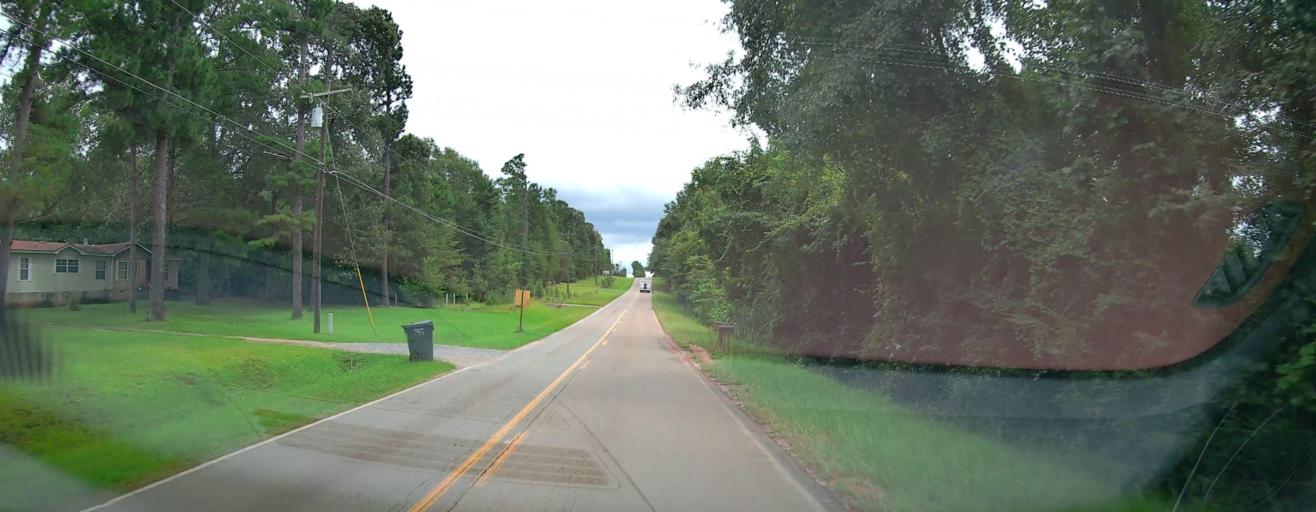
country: US
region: Georgia
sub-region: Bibb County
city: Macon
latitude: 32.7674
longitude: -83.4999
